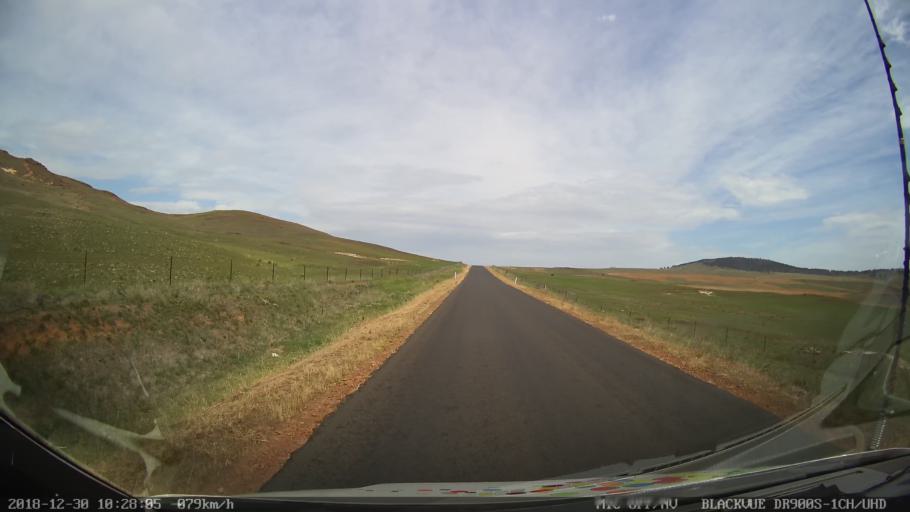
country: AU
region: New South Wales
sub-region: Snowy River
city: Berridale
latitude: -36.5080
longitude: 148.9263
